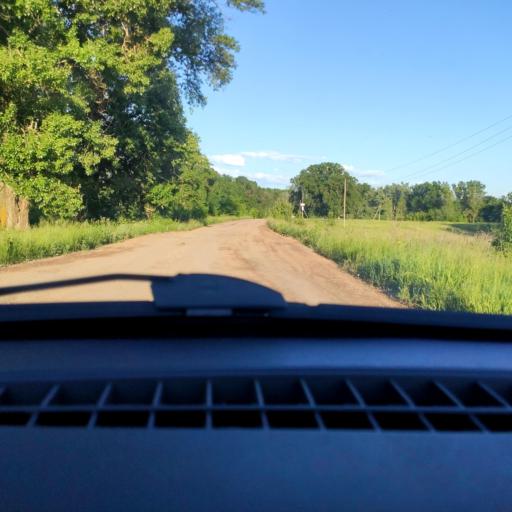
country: RU
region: Bashkortostan
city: Avdon
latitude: 54.6126
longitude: 55.6572
